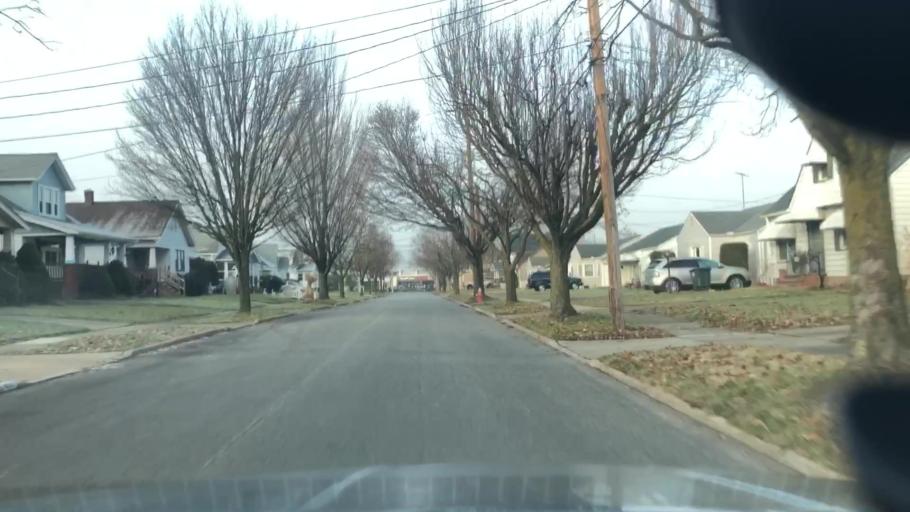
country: US
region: Ohio
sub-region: Cuyahoga County
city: Brooklyn
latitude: 41.4271
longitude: -81.7319
